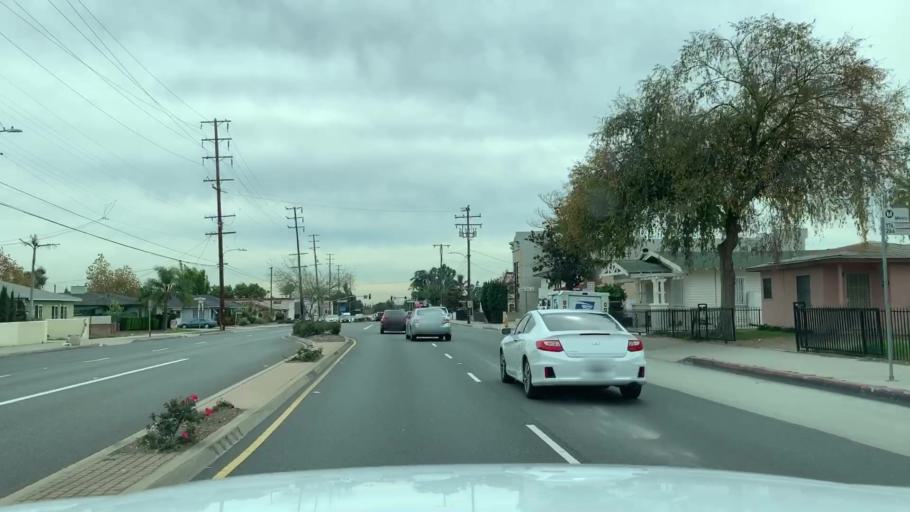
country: US
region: California
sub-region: Los Angeles County
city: Rosemead
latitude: 34.0775
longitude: -118.0732
